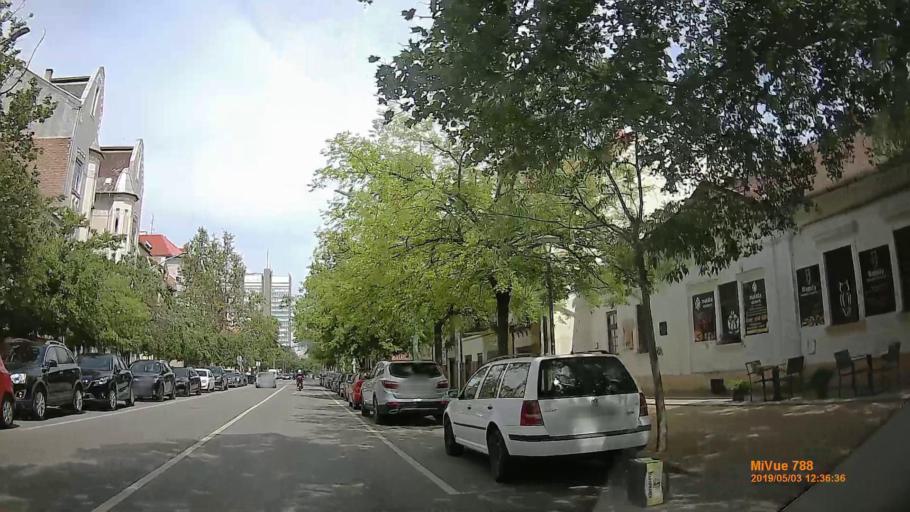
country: HU
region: Jasz-Nagykun-Szolnok
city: Szolnok
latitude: 47.1732
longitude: 20.1934
